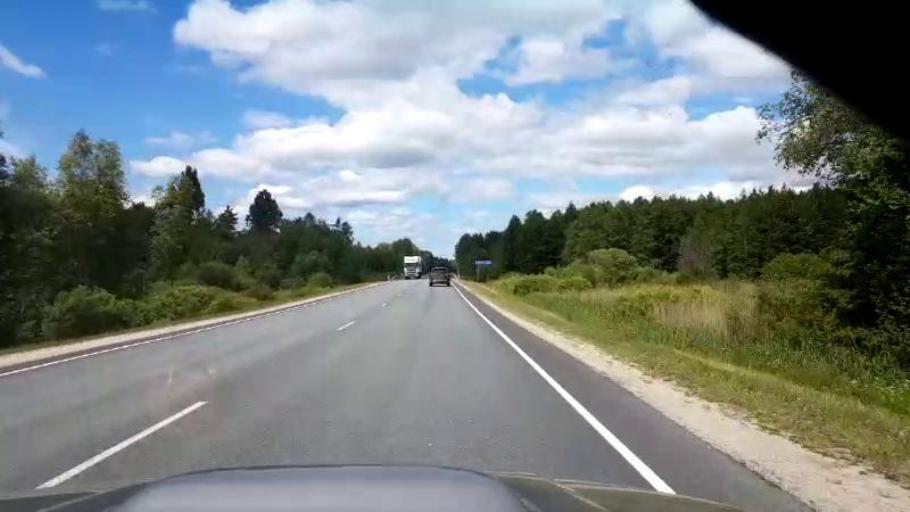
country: EE
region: Raplamaa
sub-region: Maerjamaa vald
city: Marjamaa
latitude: 59.0388
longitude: 24.4435
